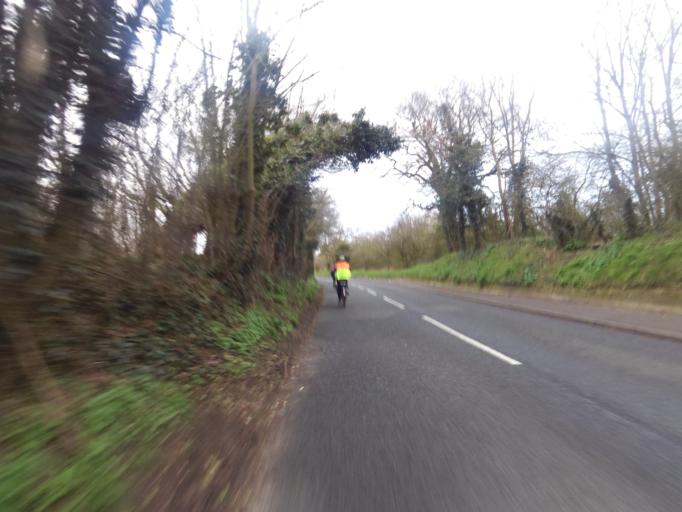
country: GB
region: England
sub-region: Suffolk
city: Ipswich
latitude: 52.0761
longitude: 1.1640
